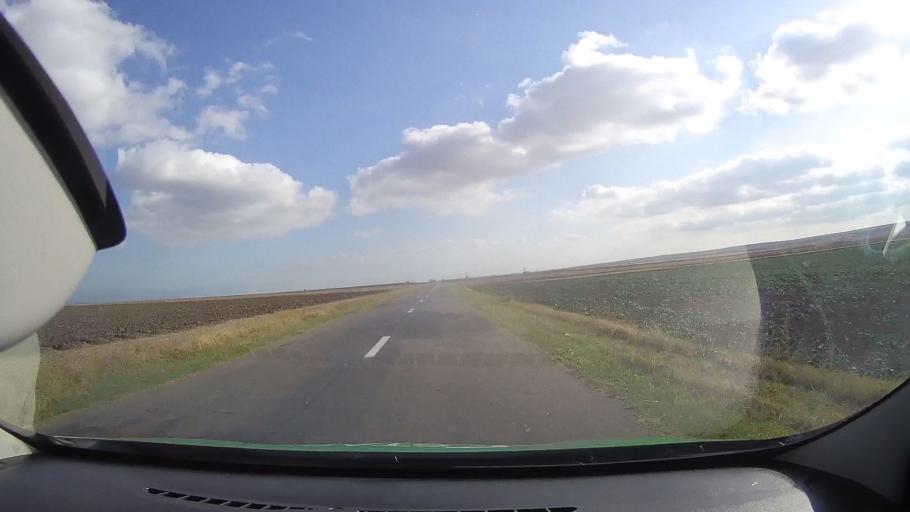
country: RO
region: Constanta
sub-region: Comuna Cogealac
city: Tariverde
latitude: 44.5568
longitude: 28.6157
